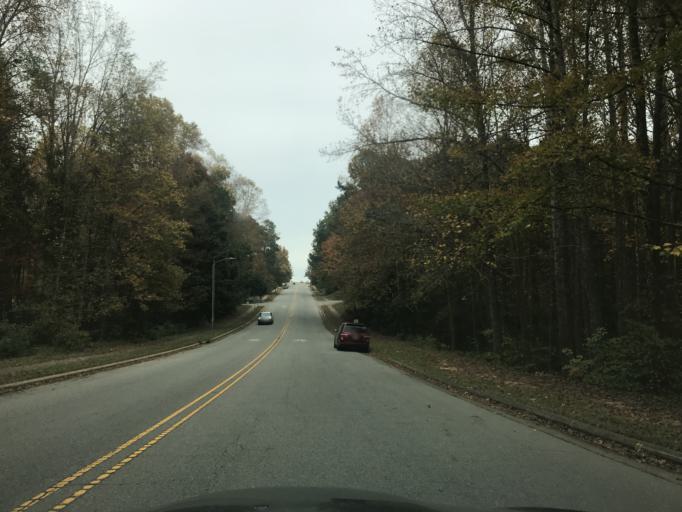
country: US
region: North Carolina
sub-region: Wake County
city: West Raleigh
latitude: 35.8817
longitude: -78.6538
